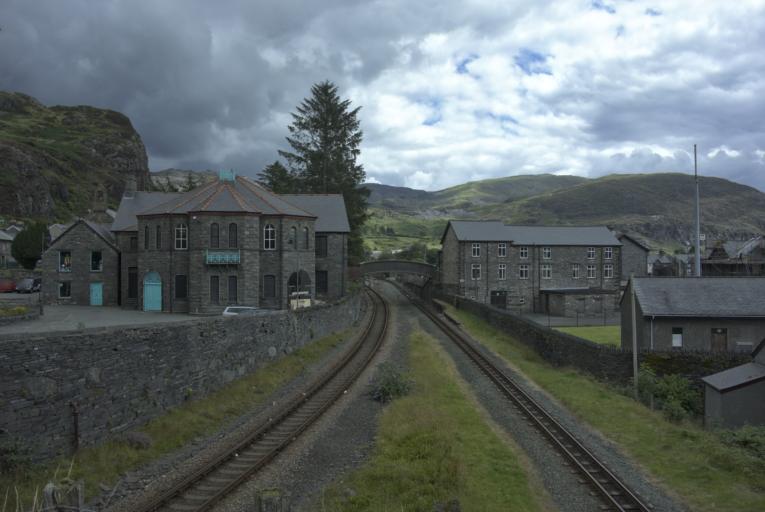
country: GB
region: Wales
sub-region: Gwynedd
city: Blaenau-Ffestiniog
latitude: 52.9949
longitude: -3.9426
